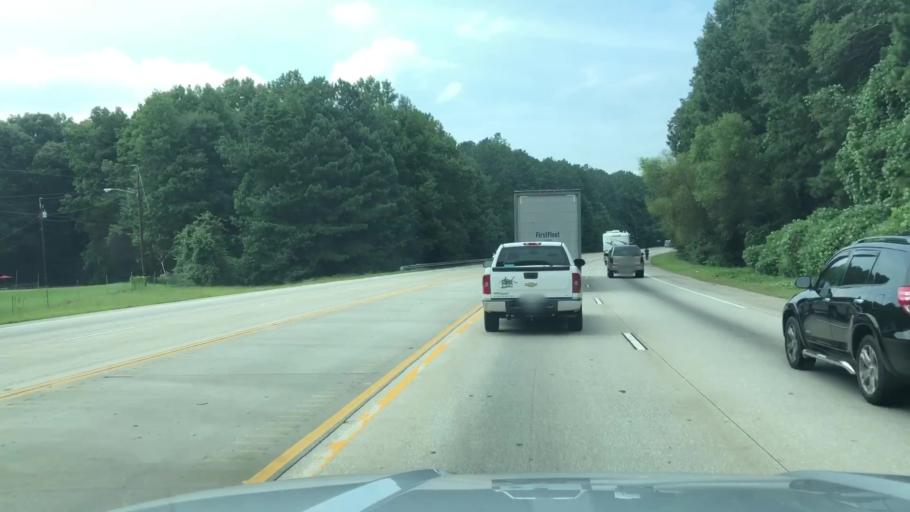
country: US
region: Georgia
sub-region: Douglas County
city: Lithia Springs
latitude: 33.7993
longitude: -84.6480
